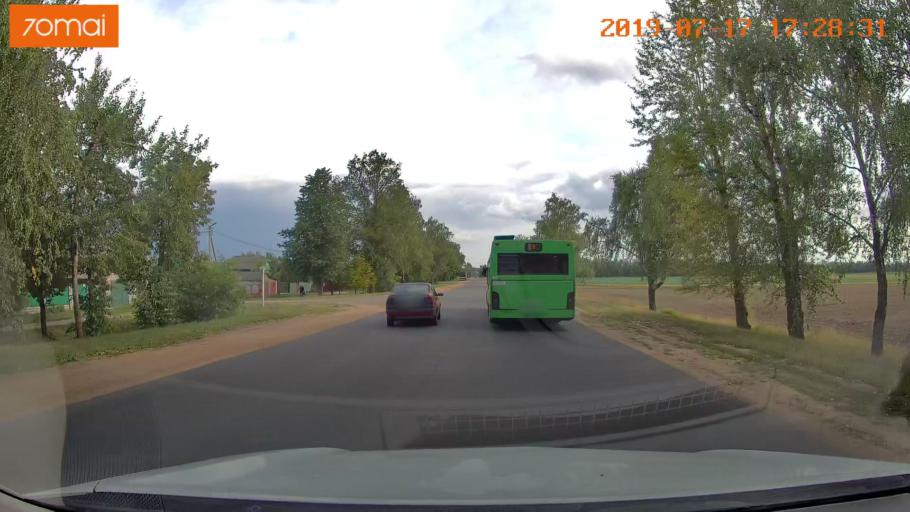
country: BY
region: Mogilev
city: Babruysk
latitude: 53.1292
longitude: 29.1667
